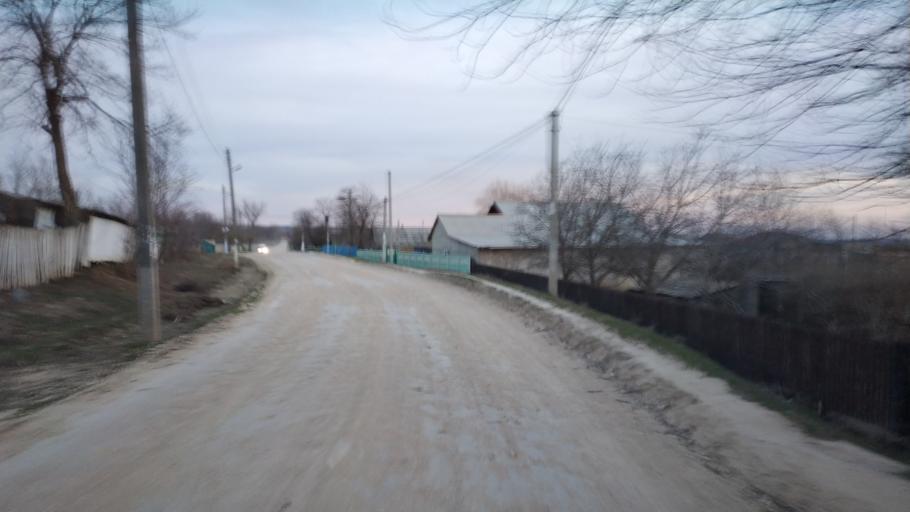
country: MD
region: Hincesti
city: Dancu
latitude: 46.7393
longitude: 28.2132
